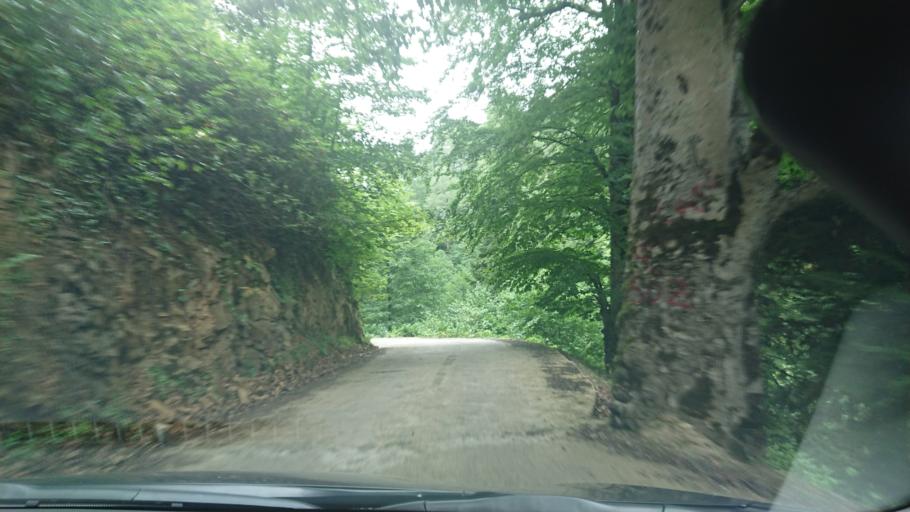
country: TR
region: Gumushane
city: Kurtun
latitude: 40.6739
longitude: 39.0434
